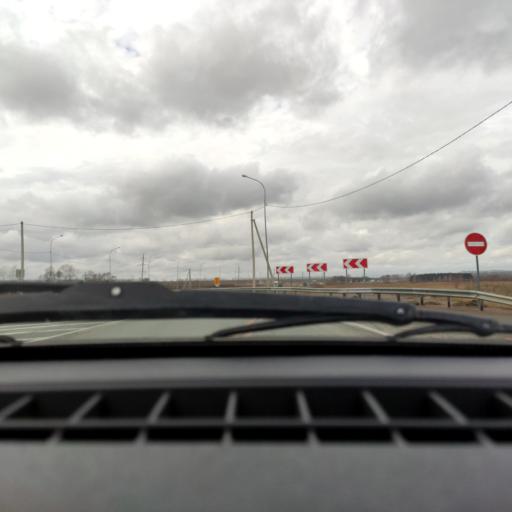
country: RU
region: Bashkortostan
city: Asanovo
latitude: 54.9101
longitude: 55.6005
